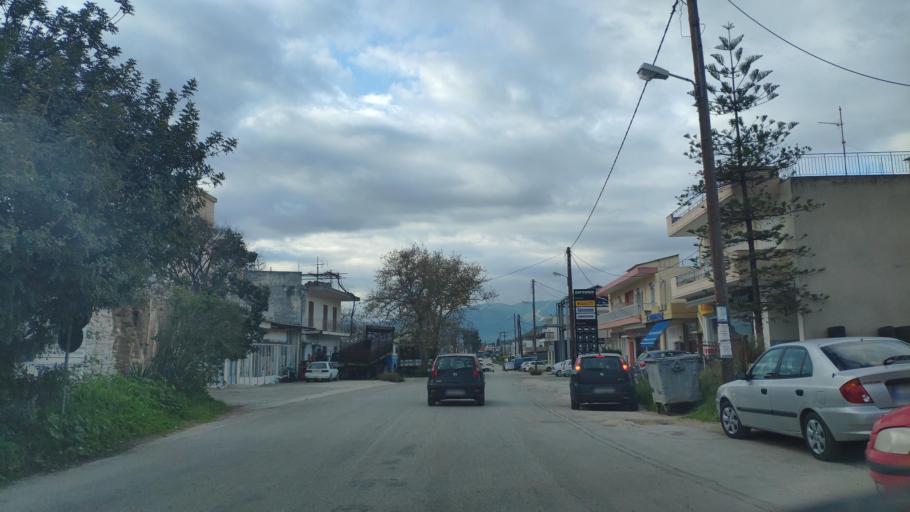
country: GR
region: Peloponnese
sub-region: Nomos Argolidos
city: Argos
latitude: 37.6270
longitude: 22.7189
